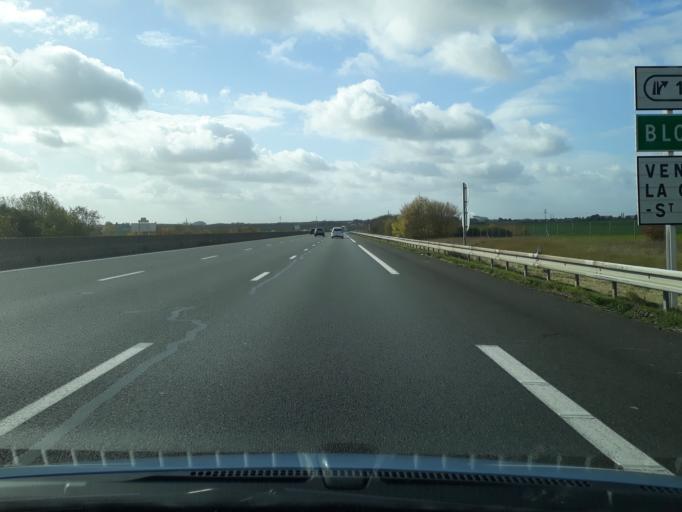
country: FR
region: Centre
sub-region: Departement du Loir-et-Cher
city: La Chaussee-Saint-Victor
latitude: 47.6351
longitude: 1.3569
